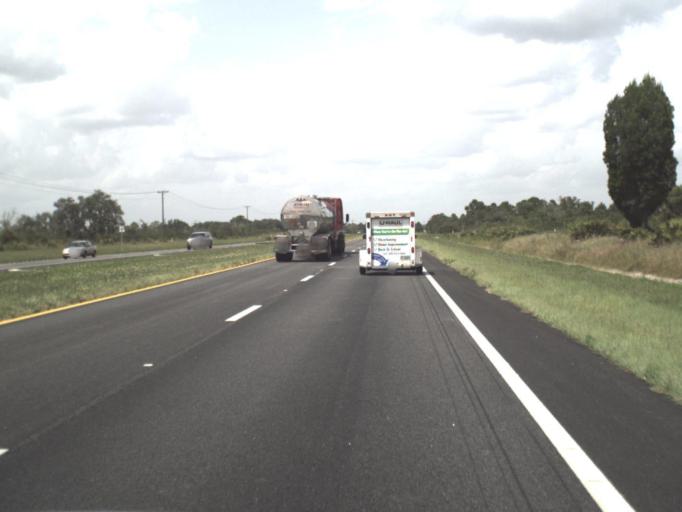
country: US
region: Florida
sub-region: Polk County
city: Frostproof
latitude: 27.6869
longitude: -81.5601
